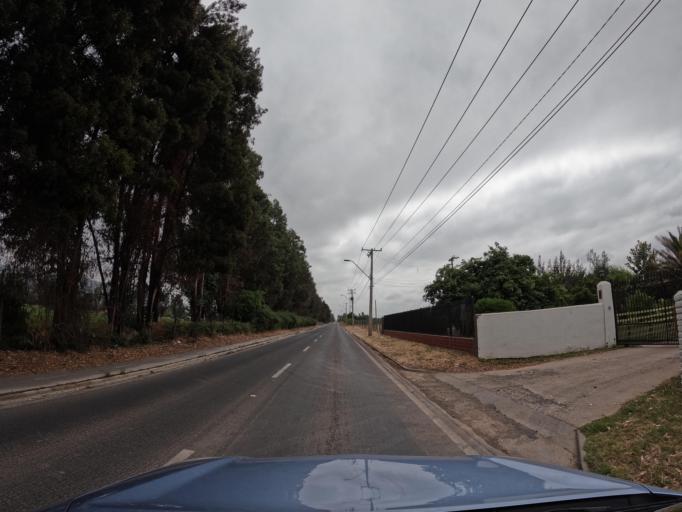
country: CL
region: O'Higgins
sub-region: Provincia de Colchagua
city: Chimbarongo
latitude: -34.7264
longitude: -71.0568
